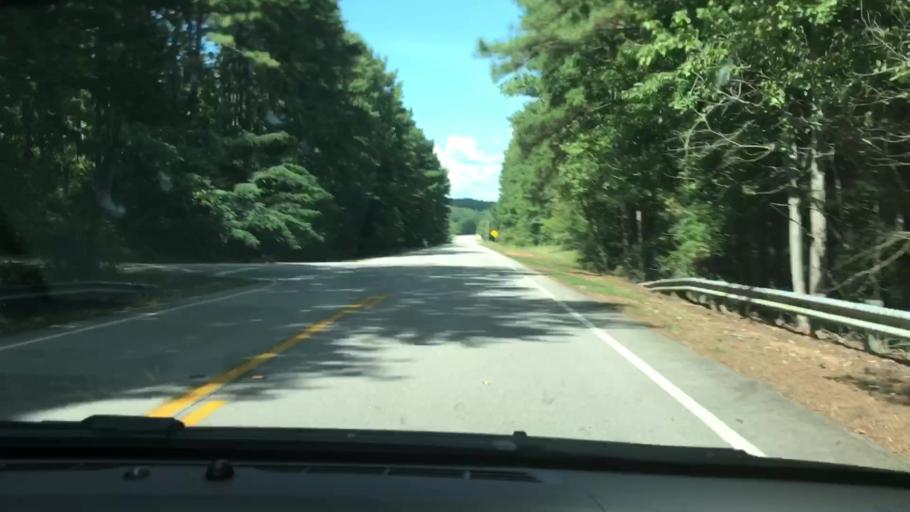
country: US
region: Georgia
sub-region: Troup County
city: La Grange
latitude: 33.1274
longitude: -85.0893
